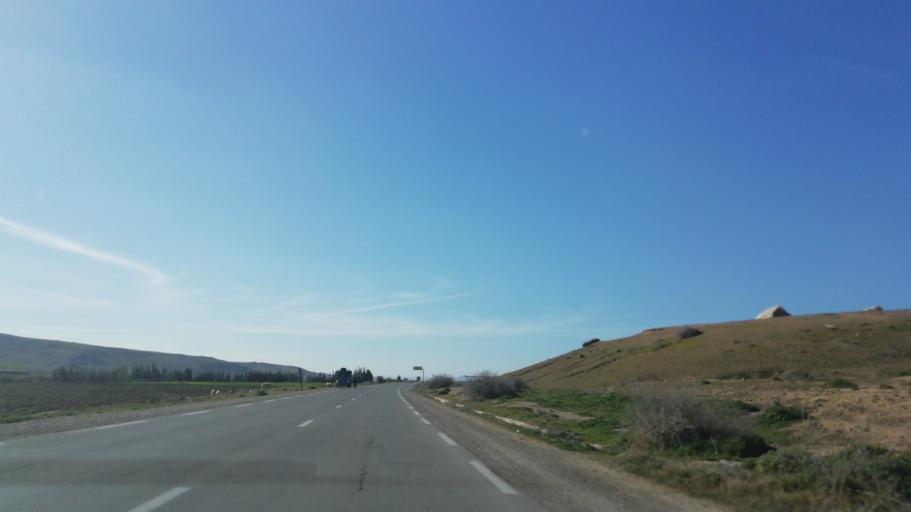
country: DZ
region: Mascara
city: Oued el Abtal
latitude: 35.4500
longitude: 0.7876
